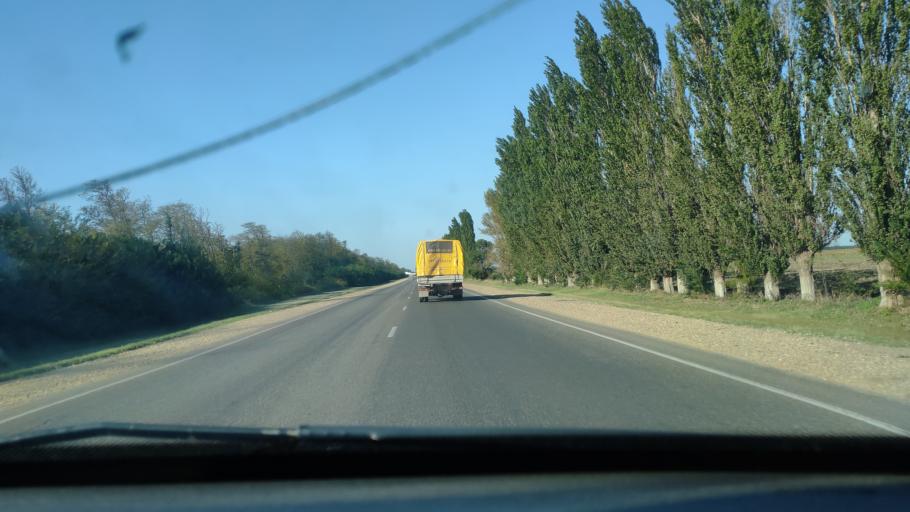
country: RU
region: Krasnodarskiy
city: Novotitarovskaya
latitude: 45.2658
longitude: 39.0018
